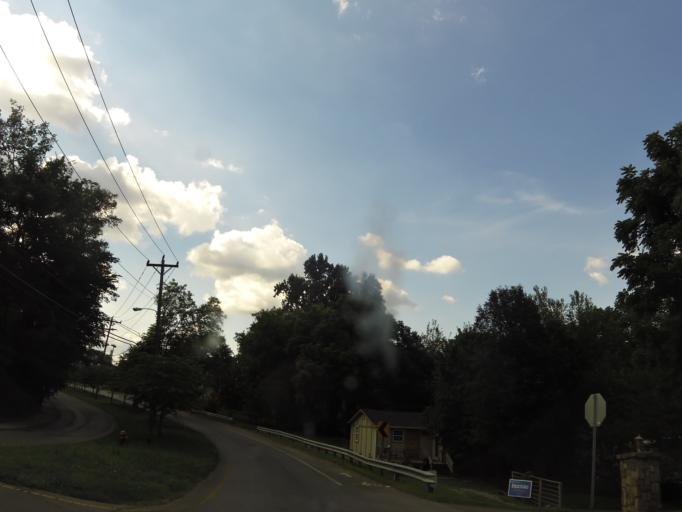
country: US
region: Tennessee
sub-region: Davidson County
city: Nashville
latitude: 36.2032
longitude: -86.7226
